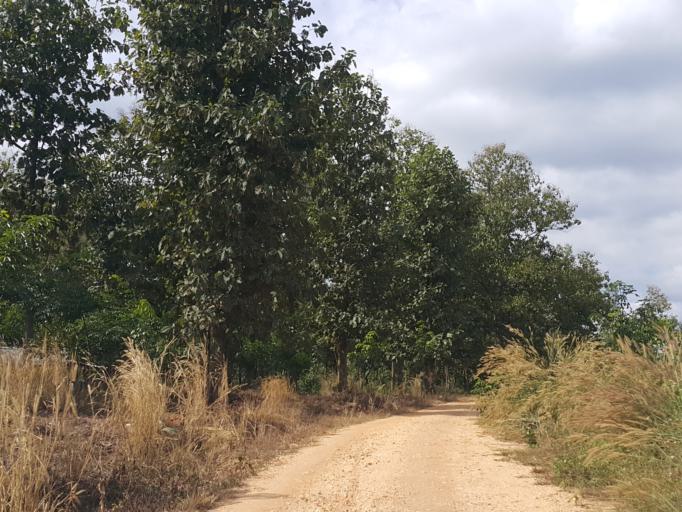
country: TH
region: Lampang
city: Hang Chat
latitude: 18.4886
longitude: 99.4039
